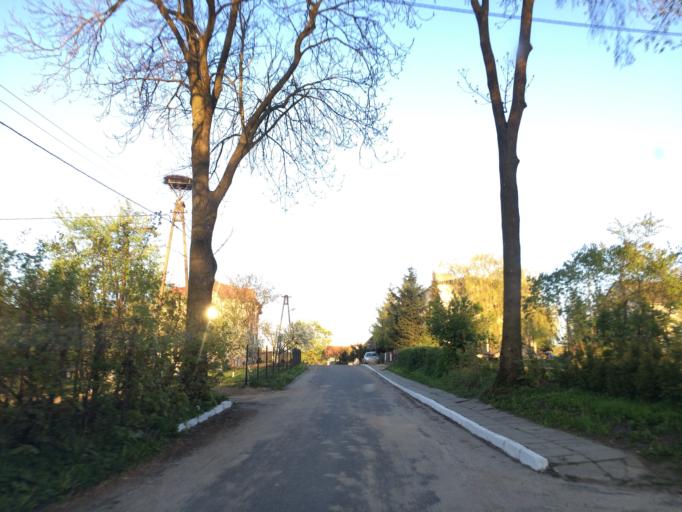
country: PL
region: Warmian-Masurian Voivodeship
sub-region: Powiat ilawski
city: Lubawa
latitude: 53.5258
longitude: 19.8739
